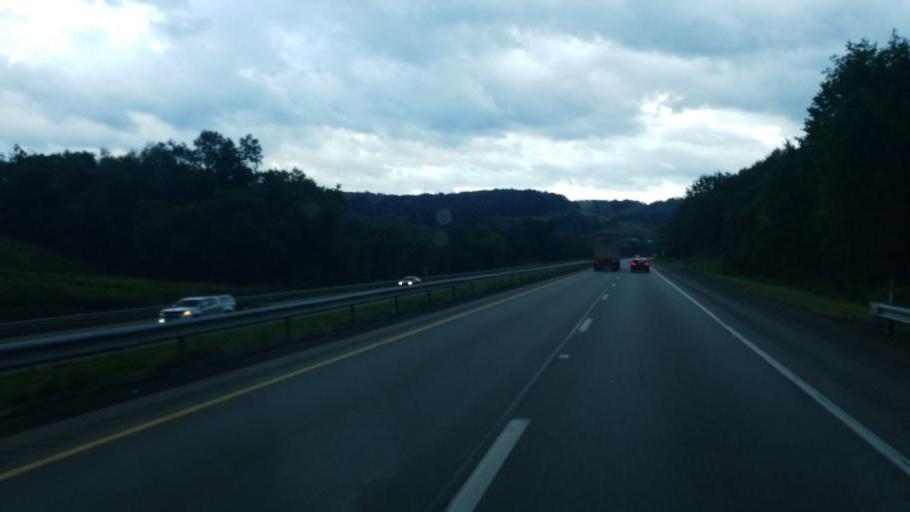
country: US
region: Pennsylvania
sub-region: Butler County
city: Zelienople
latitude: 40.8543
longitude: -80.1058
